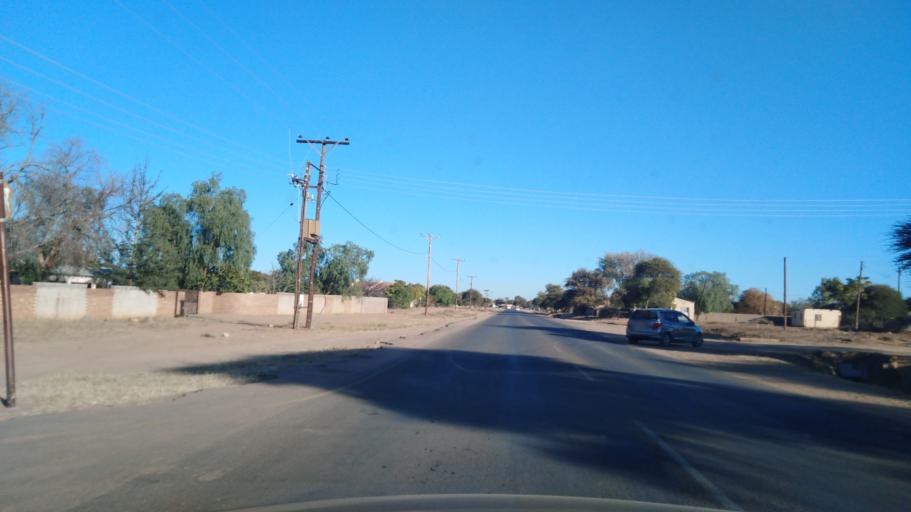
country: BW
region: Central
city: Mahalapye
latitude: -23.0946
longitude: 26.8265
